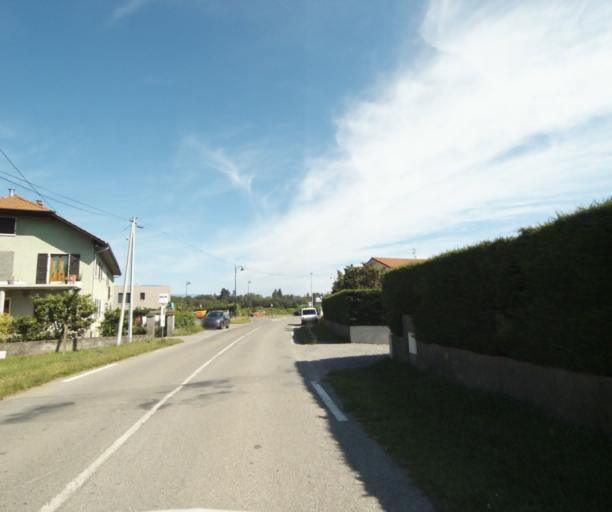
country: FR
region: Rhone-Alpes
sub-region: Departement de la Haute-Savoie
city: Thonon-les-Bains
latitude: 46.3864
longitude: 6.5021
